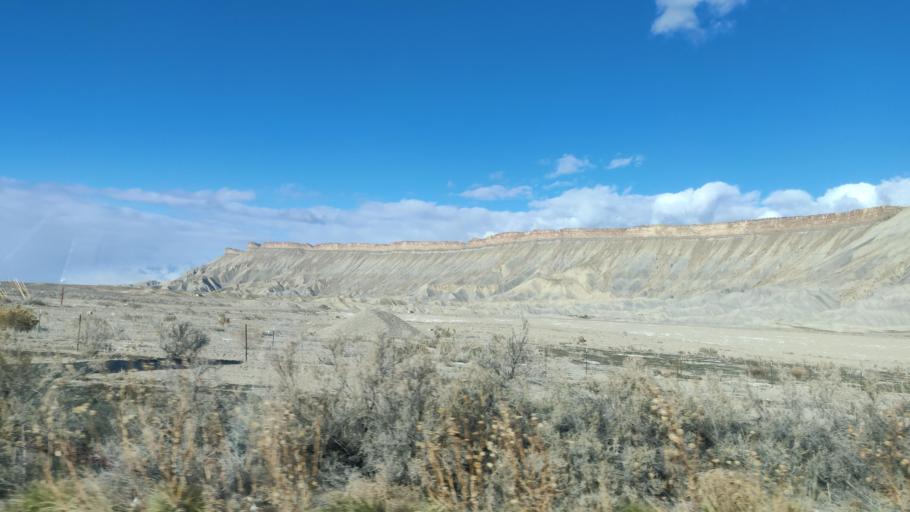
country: US
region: Colorado
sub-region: Mesa County
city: Clifton
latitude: 39.1097
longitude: -108.4241
